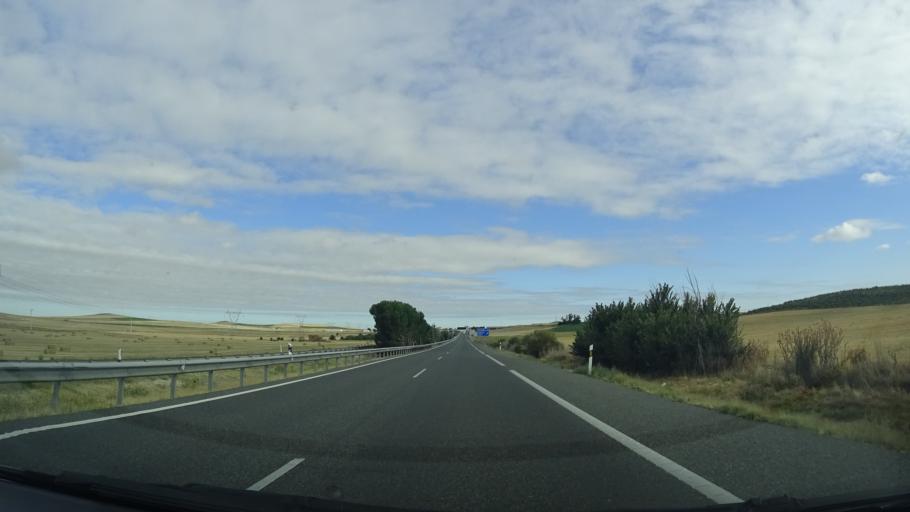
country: ES
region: Castille and Leon
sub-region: Provincia de Valladolid
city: Ataquines
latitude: 41.1675
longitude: -4.8005
